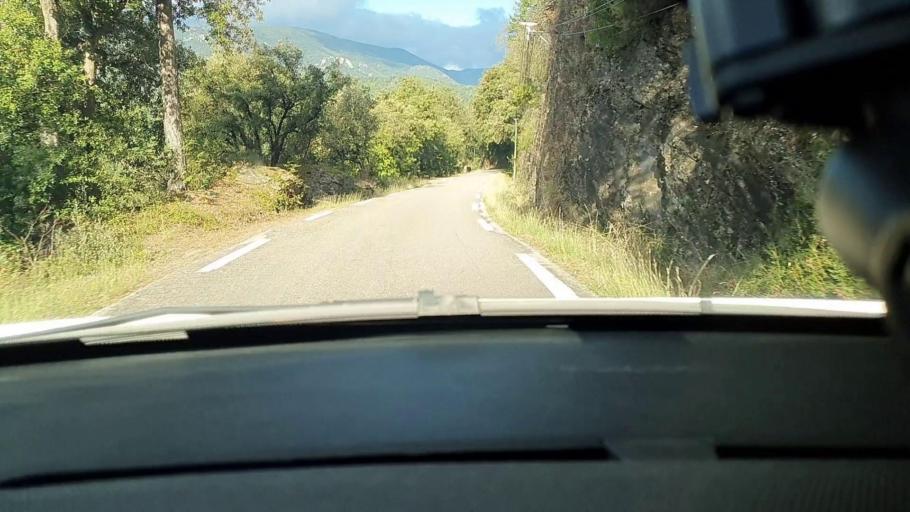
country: FR
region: Languedoc-Roussillon
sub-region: Departement du Gard
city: Besseges
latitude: 44.3641
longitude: 4.0000
